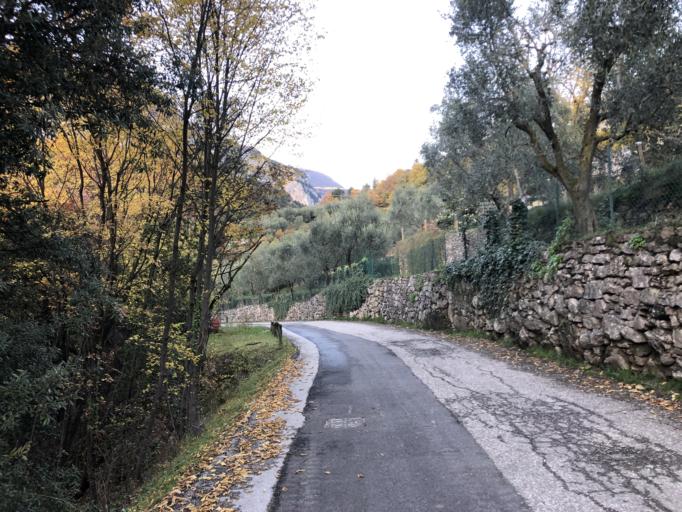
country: IT
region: Trentino-Alto Adige
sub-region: Provincia di Trento
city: Arco
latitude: 45.9317
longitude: 10.8854
